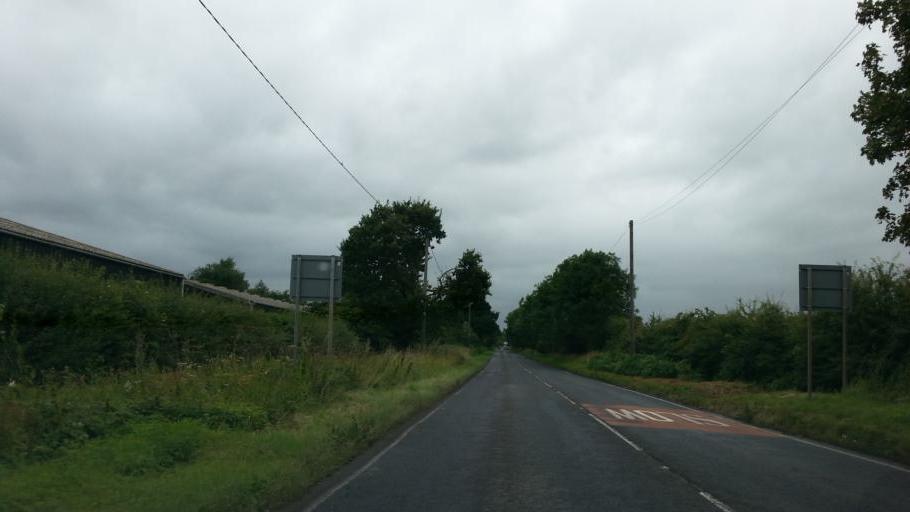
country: GB
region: England
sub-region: Nottinghamshire
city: Blidworth
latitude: 53.0486
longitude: -1.0885
